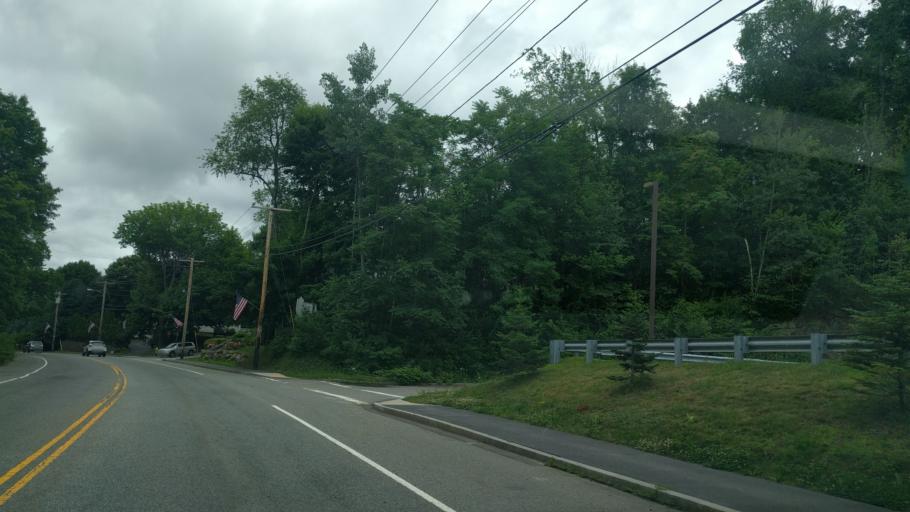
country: US
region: Massachusetts
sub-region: Worcester County
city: Worcester
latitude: 42.2365
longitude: -71.8012
